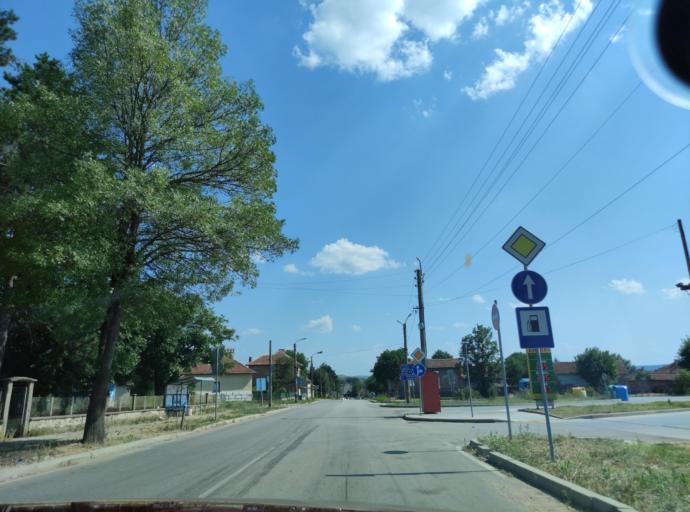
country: BG
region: Pleven
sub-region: Obshtina Cherven Bryag
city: Koynare
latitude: 43.3309
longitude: 24.0669
